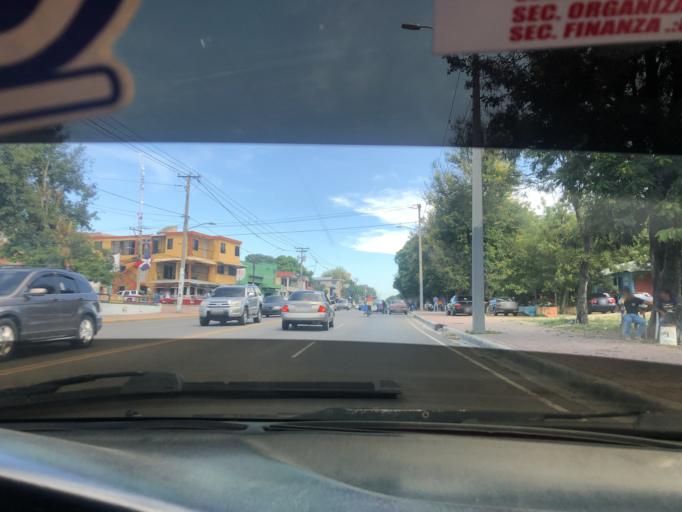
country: DO
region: Santiago
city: Santiago de los Caballeros
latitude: 19.4371
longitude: -70.6981
